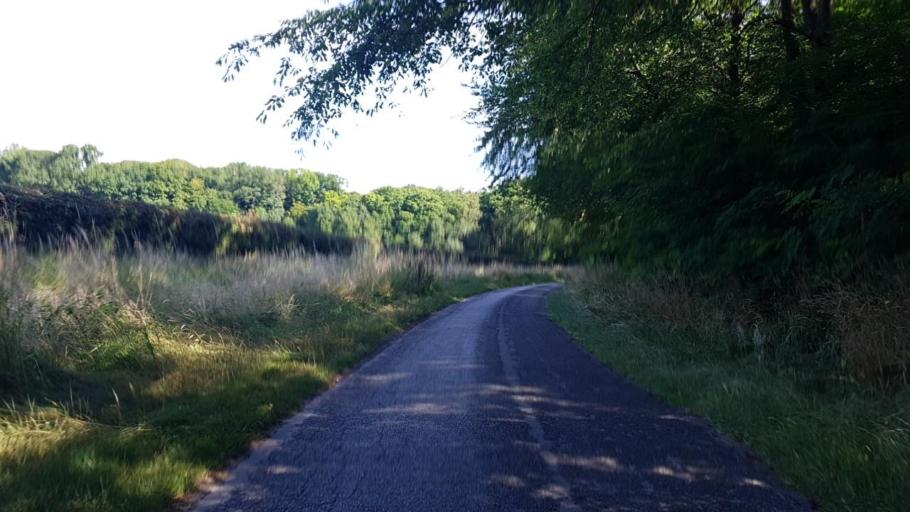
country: FR
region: Picardie
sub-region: Departement de l'Oise
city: Pontpoint
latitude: 49.2932
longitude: 2.6458
